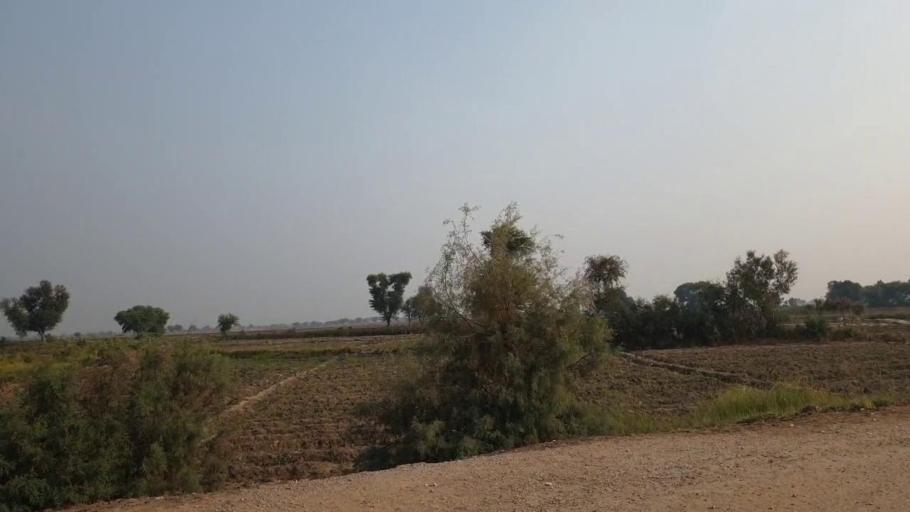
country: PK
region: Sindh
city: Bhan
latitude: 26.4733
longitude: 67.7266
